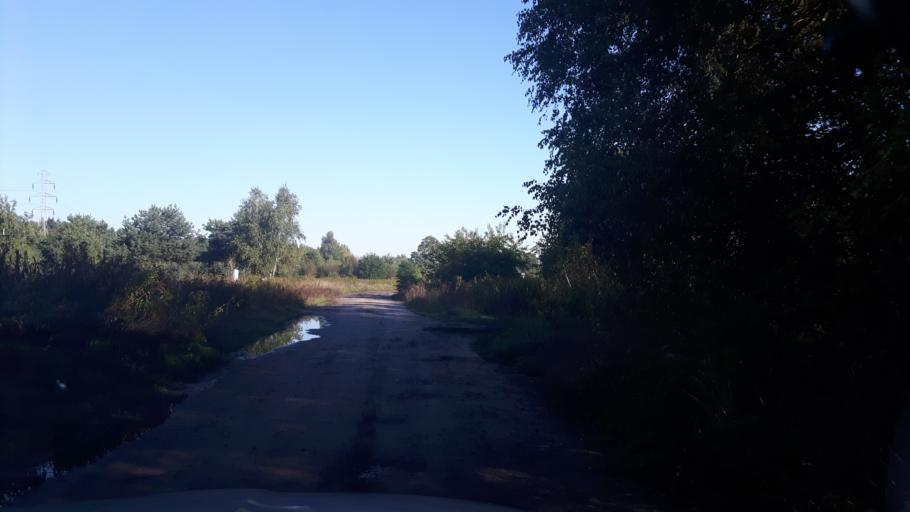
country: PL
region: Masovian Voivodeship
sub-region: Powiat legionowski
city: Stanislawow Pierwszy
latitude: 52.3646
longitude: 21.0373
